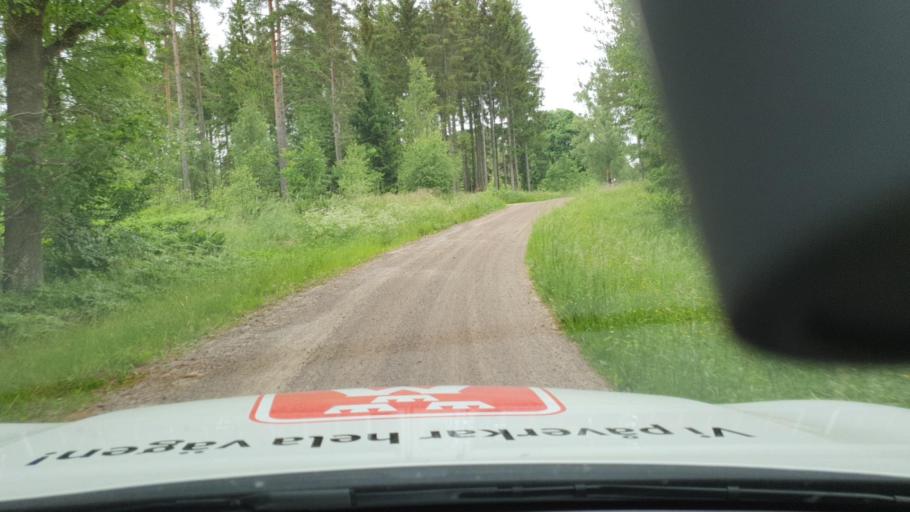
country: SE
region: Vaestra Goetaland
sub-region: Hjo Kommun
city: Hjo
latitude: 58.3887
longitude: 14.3429
